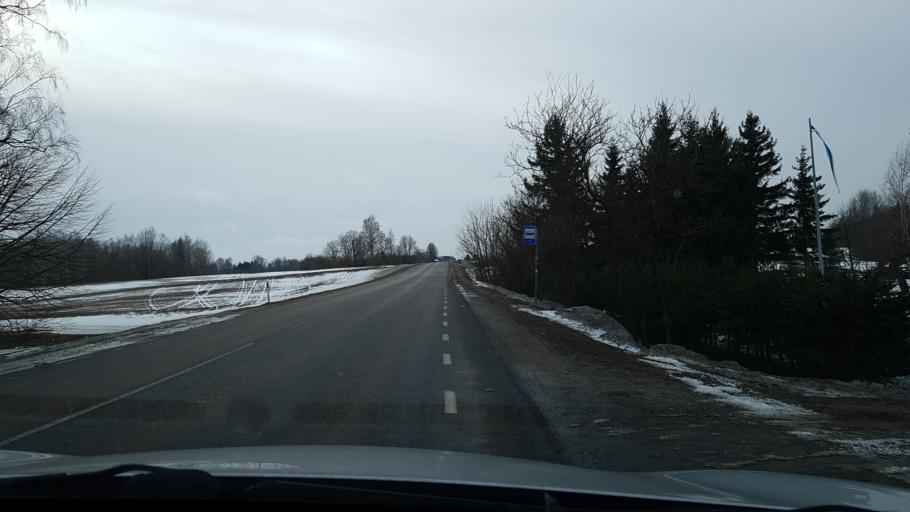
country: EE
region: Tartu
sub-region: Noo vald
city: Noo
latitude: 58.2191
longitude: 26.6244
